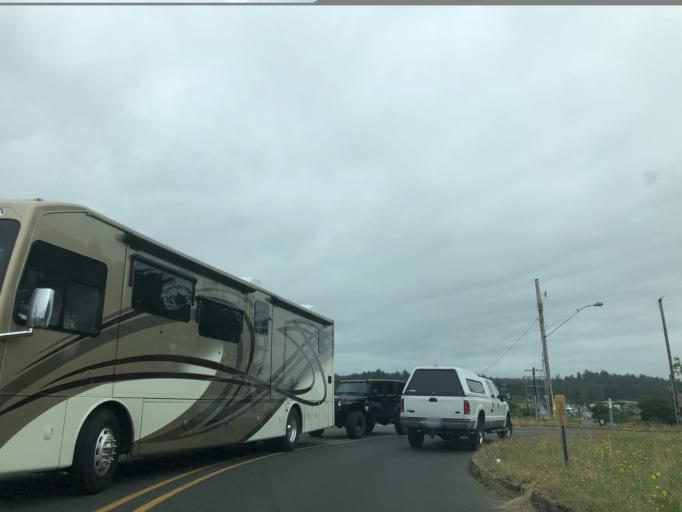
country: US
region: Oregon
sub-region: Lincoln County
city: Newport
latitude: 44.6176
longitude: -124.0508
